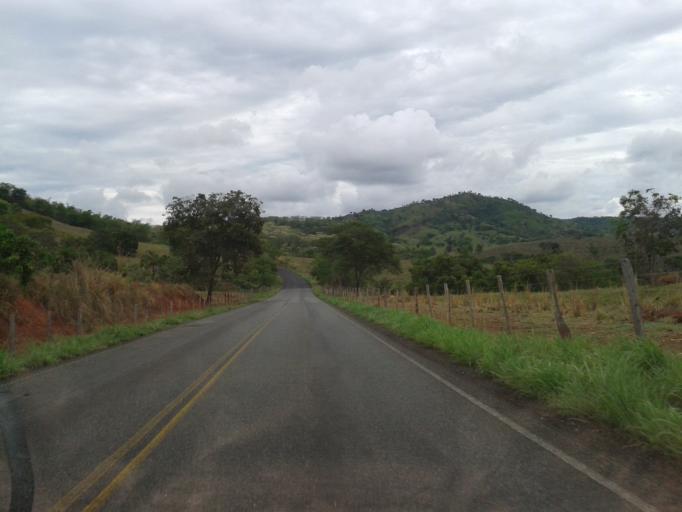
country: BR
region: Goias
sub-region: Caldas Novas
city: Caldas Novas
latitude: -18.0572
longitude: -48.7058
